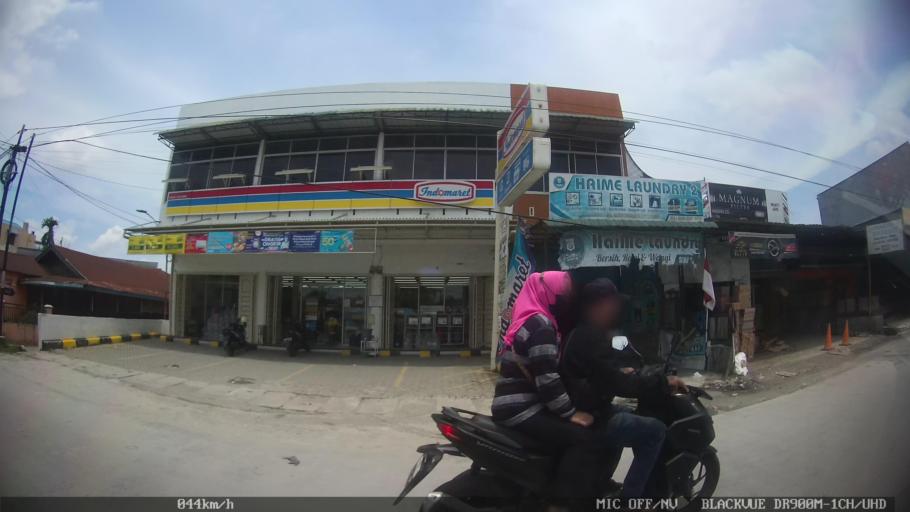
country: ID
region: North Sumatra
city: Labuhan Deli
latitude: 3.6932
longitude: 98.6789
